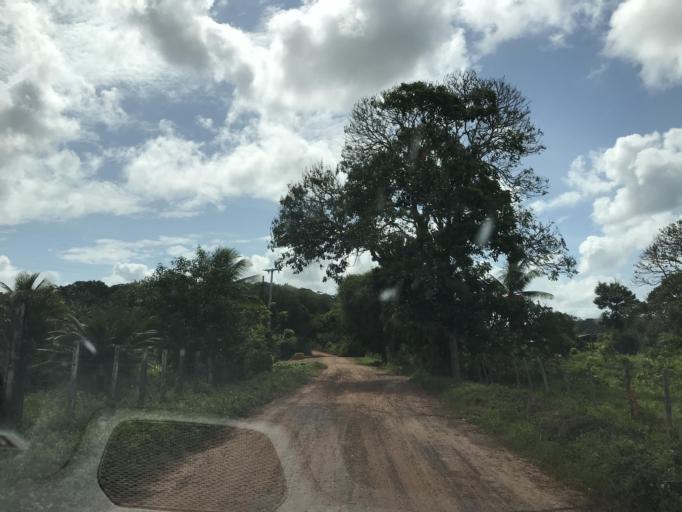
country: BR
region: Bahia
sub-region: Entre Rios
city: Entre Rios
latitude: -12.1609
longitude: -38.0774
